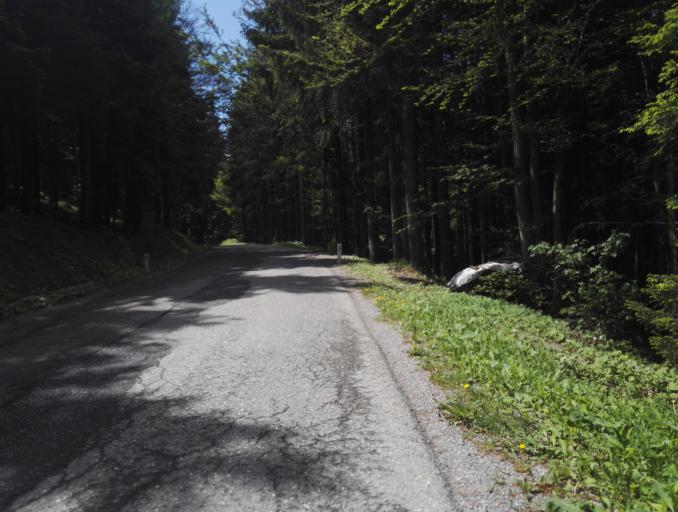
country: AT
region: Styria
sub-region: Politischer Bezirk Weiz
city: Stenzengreith
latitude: 47.2067
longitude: 15.4865
